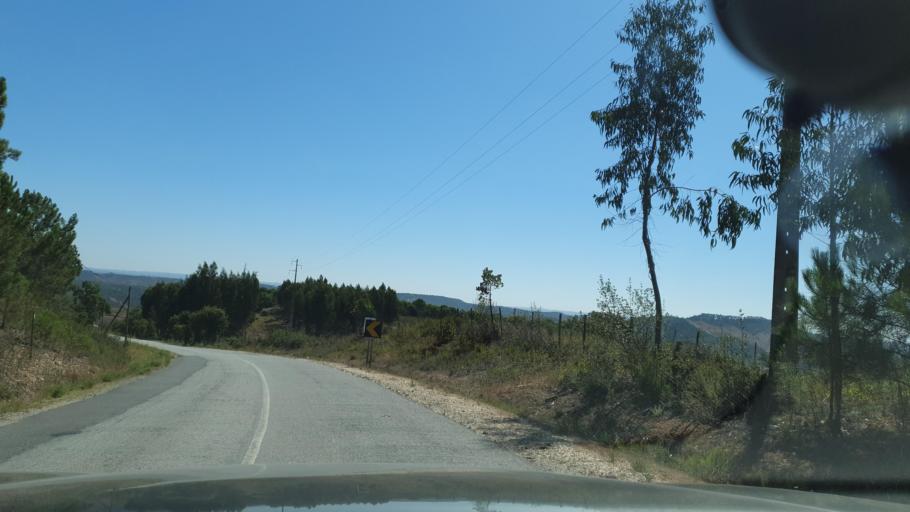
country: PT
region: Beja
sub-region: Odemira
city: Sao Teotonio
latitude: 37.4998
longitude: -8.6616
